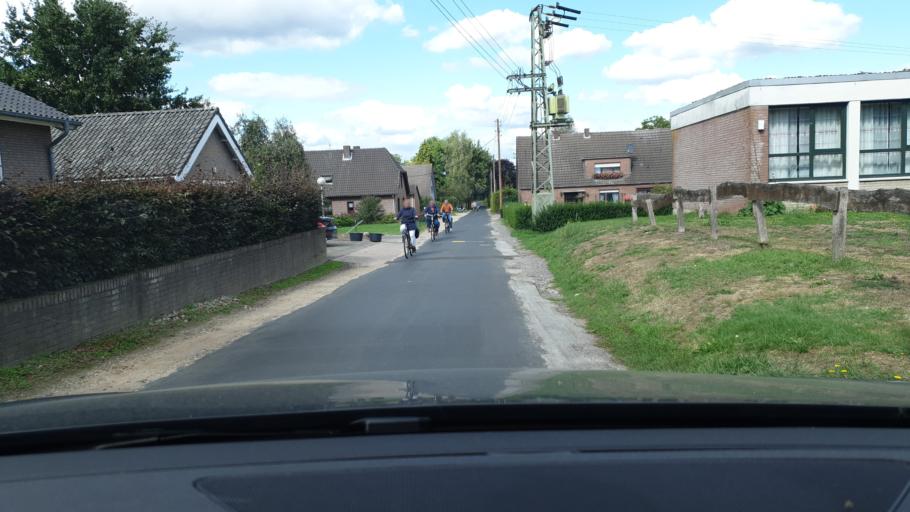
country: NL
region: Gelderland
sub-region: Gemeente Groesbeek
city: Bredeweg
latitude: 51.7493
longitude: 5.9577
